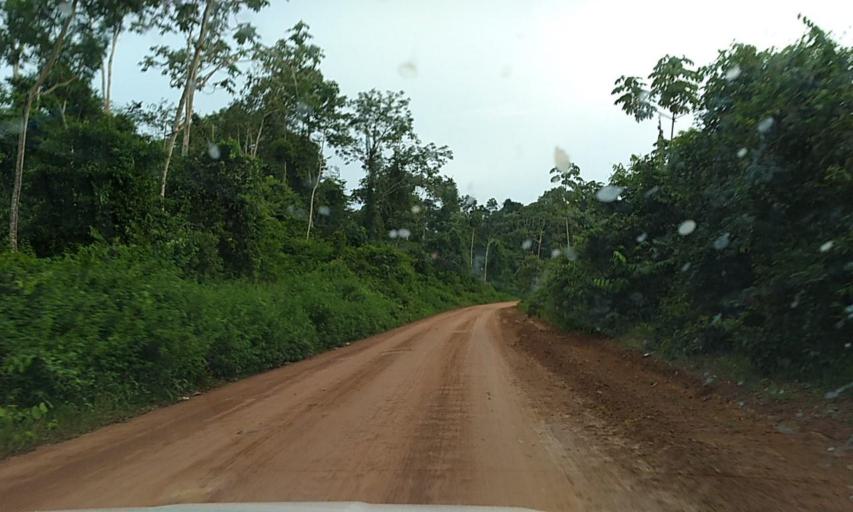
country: BR
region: Para
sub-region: Senador Jose Porfirio
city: Senador Jose Porfirio
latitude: -2.7121
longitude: -51.8045
